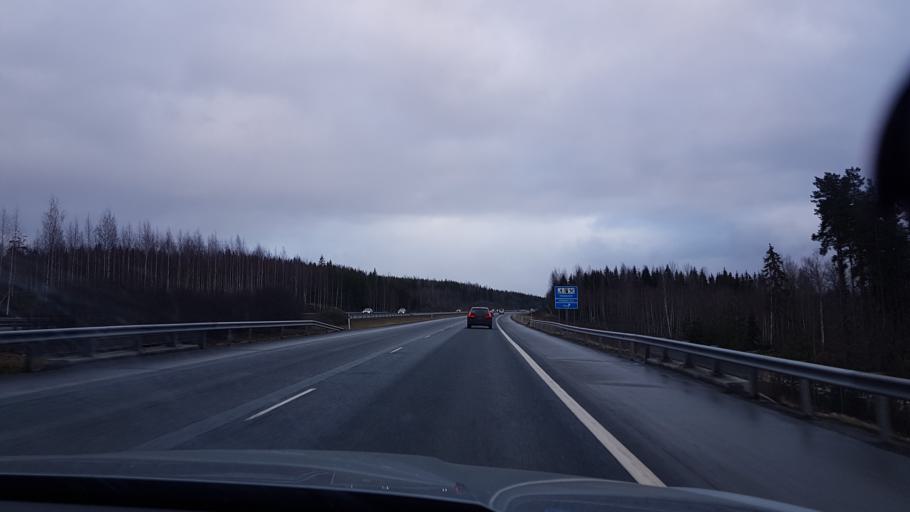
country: FI
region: Pirkanmaa
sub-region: Etelae-Pirkanmaa
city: Viiala
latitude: 61.2684
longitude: 23.8227
